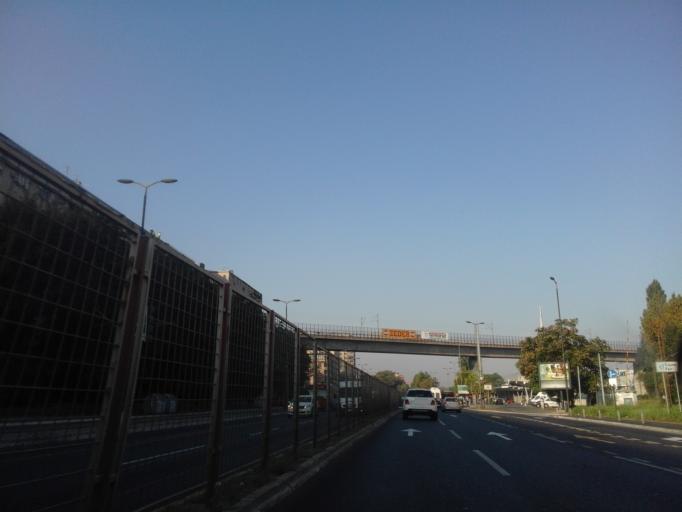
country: RS
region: Central Serbia
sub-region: Belgrade
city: Savski Venac
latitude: 44.7971
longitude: 20.4442
